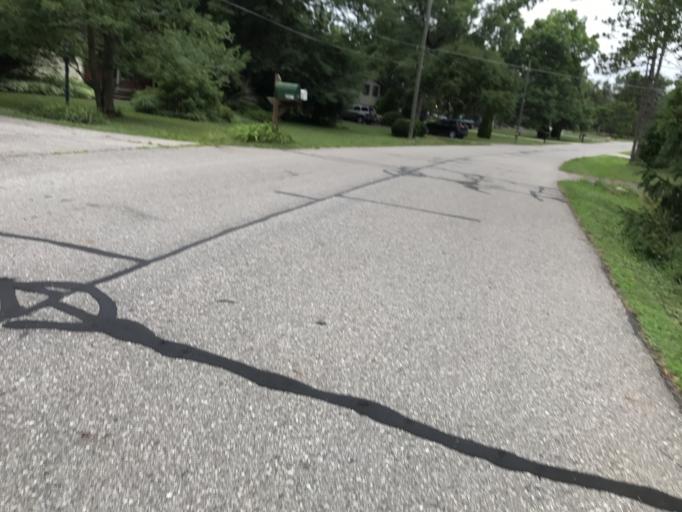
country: US
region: Michigan
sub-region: Oakland County
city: Farmington
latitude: 42.4722
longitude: -83.3305
